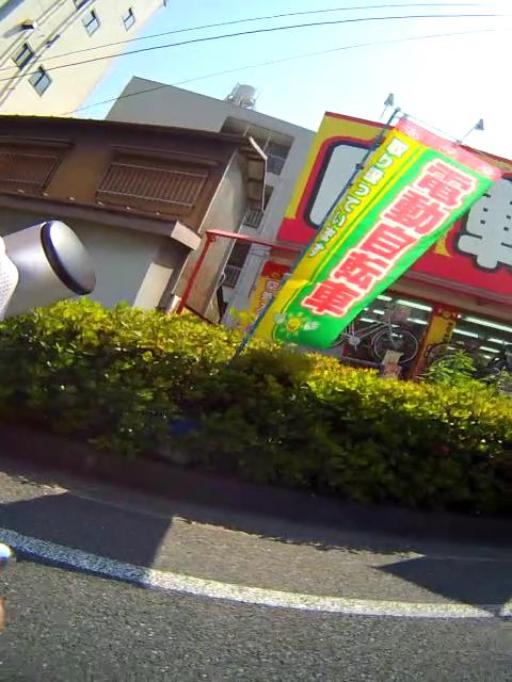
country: JP
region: Osaka
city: Yao
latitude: 34.6228
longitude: 135.5491
